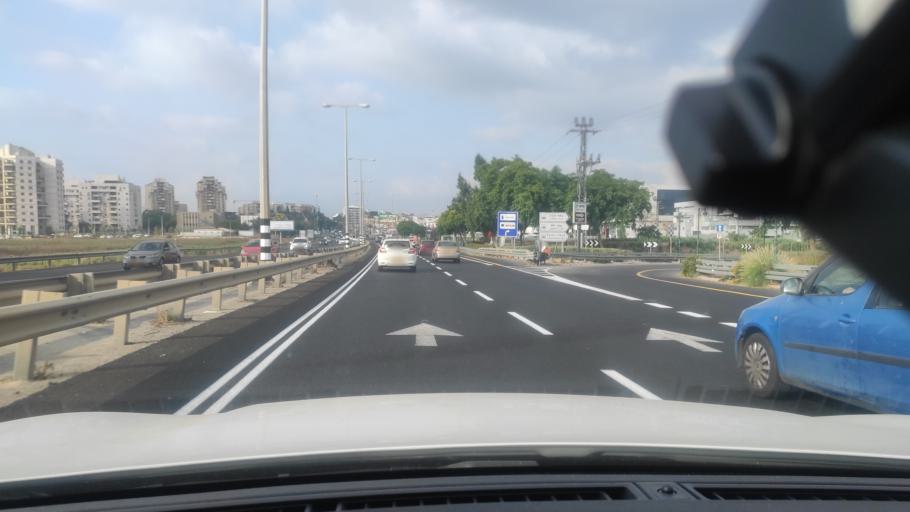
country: IL
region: Central District
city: Petah Tiqwa
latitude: 32.1063
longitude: 34.9000
